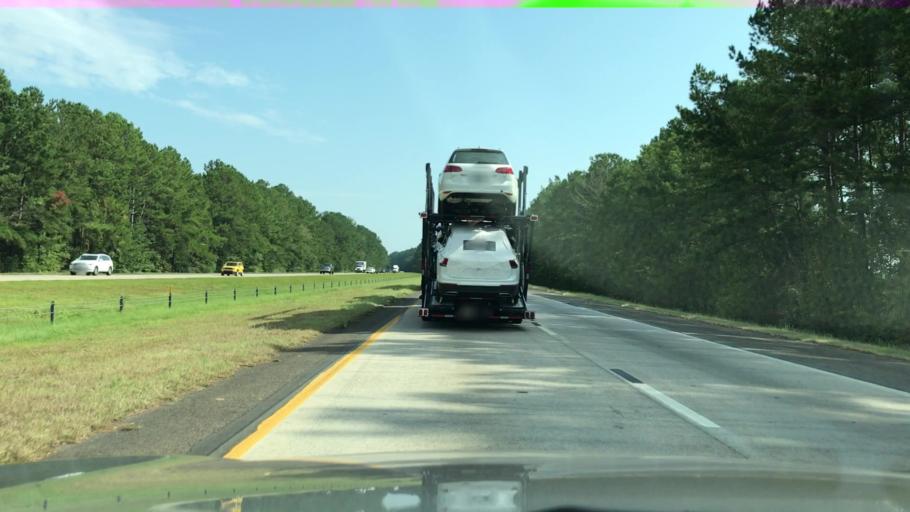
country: US
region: South Carolina
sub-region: Colleton County
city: Walterboro
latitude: 32.8169
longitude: -80.7586
